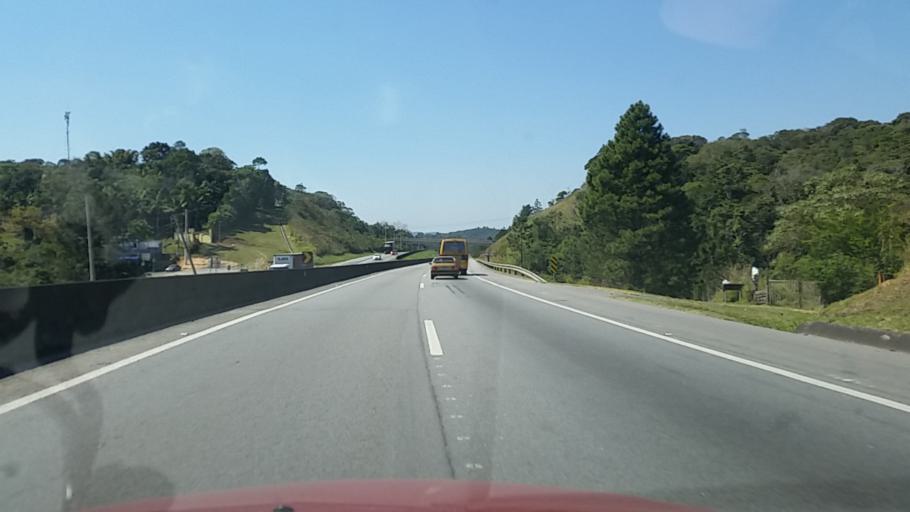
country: BR
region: Sao Paulo
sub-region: Juquitiba
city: Juquitiba
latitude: -23.9580
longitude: -47.1146
